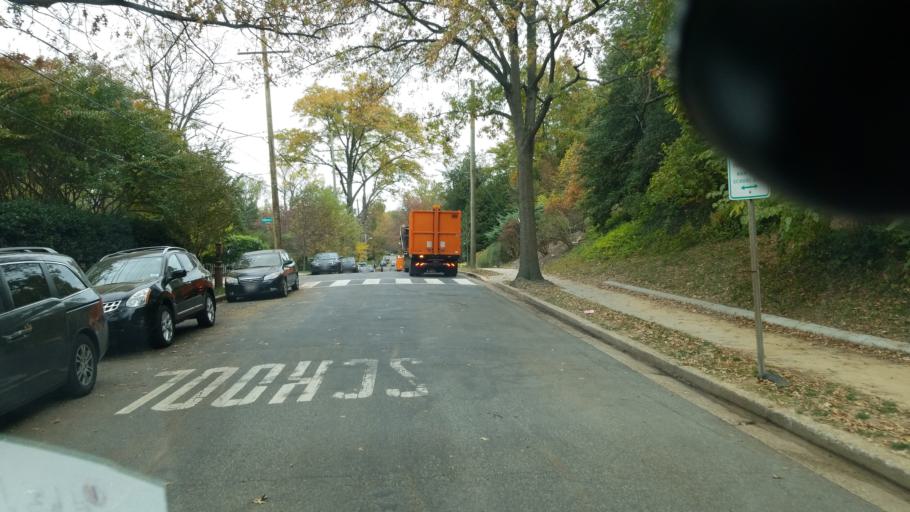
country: US
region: Maryland
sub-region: Montgomery County
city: Chevy Chase
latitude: 38.9674
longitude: -77.0691
